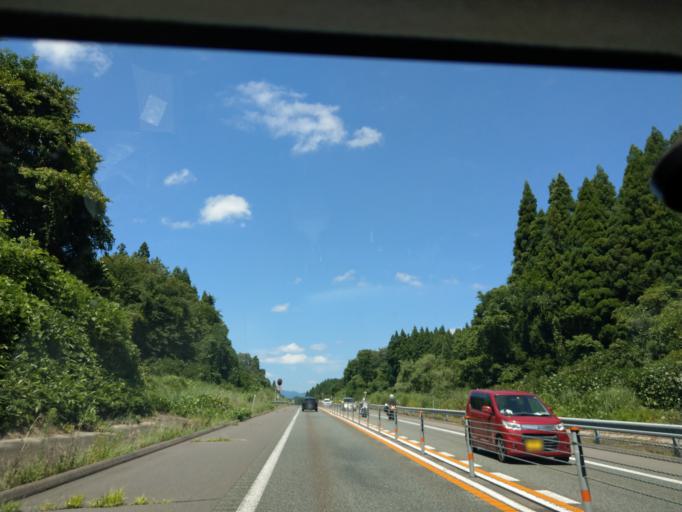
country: JP
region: Akita
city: Akita
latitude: 39.6829
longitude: 140.1857
